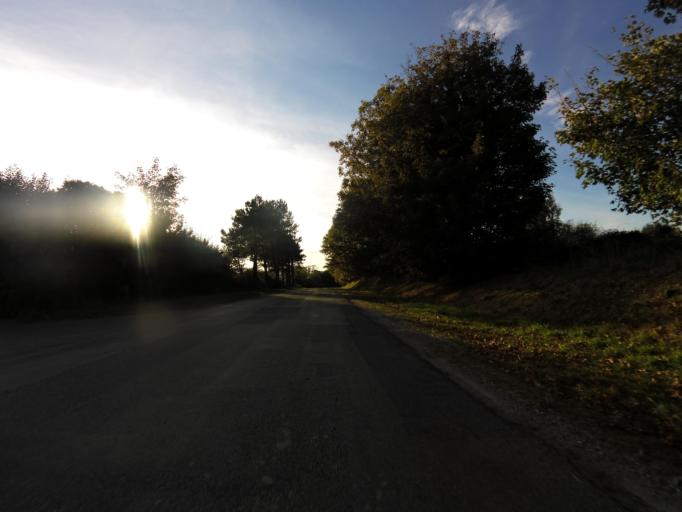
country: FR
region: Brittany
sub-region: Departement du Morbihan
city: Sulniac
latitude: 47.6670
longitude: -2.5705
